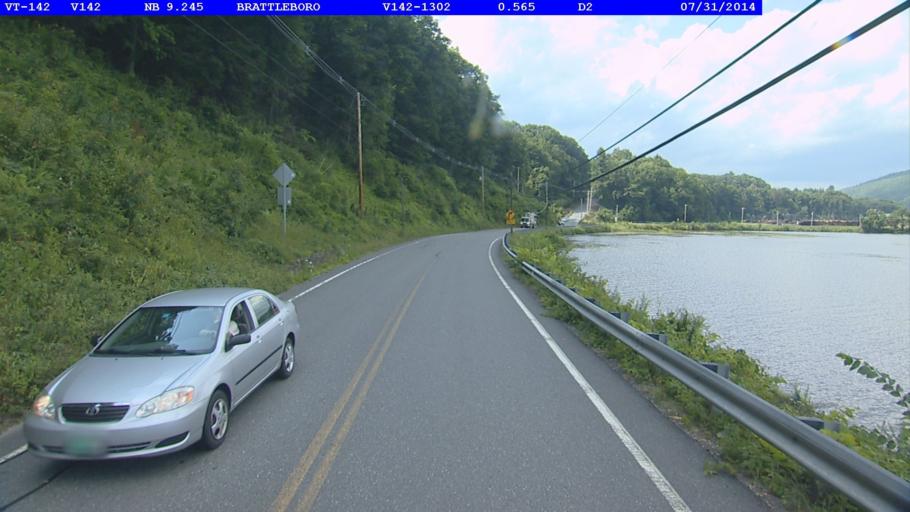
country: US
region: Vermont
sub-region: Windham County
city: Brattleboro
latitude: 42.8311
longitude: -72.5528
